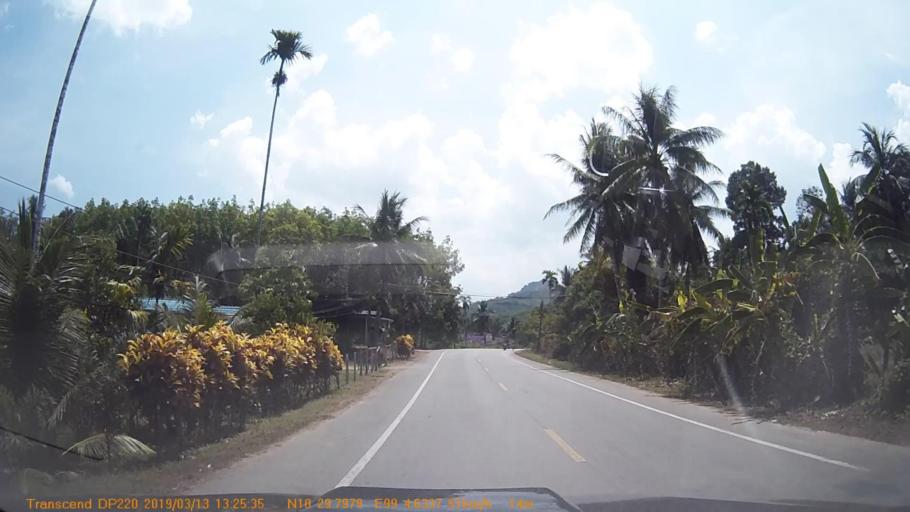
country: TH
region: Chumphon
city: Chumphon
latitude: 10.4993
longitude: 99.0781
